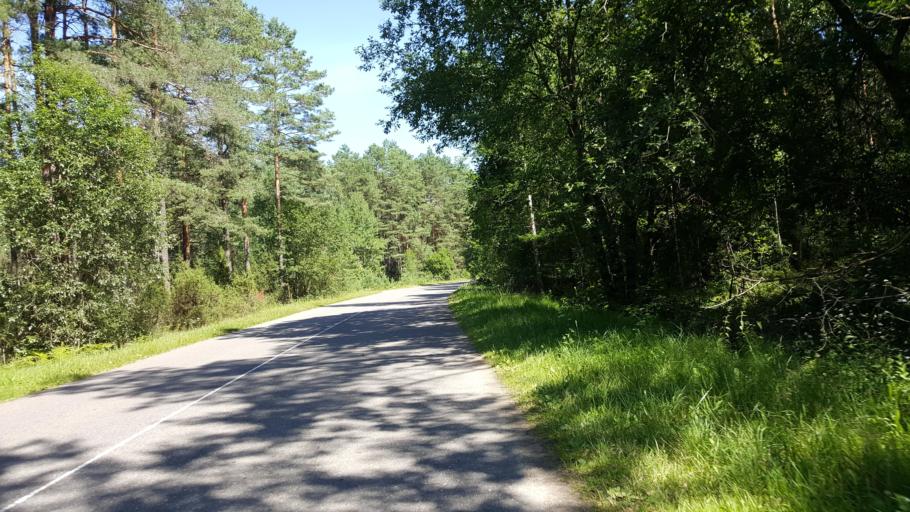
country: BY
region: Brest
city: Pruzhany
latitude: 52.5276
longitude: 24.1778
